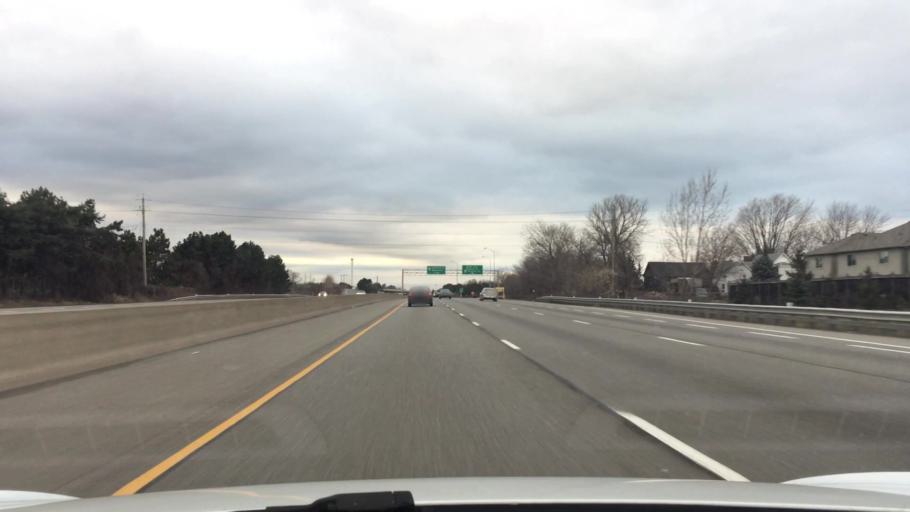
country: CA
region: Ontario
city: Oakville
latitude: 43.1946
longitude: -79.5440
